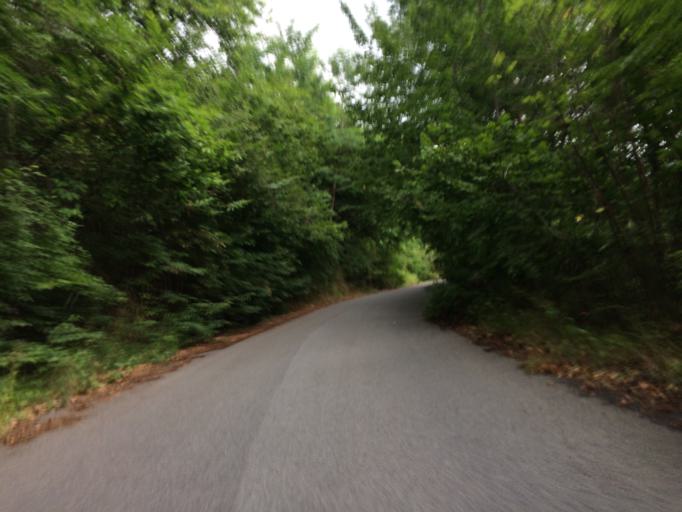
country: IT
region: Liguria
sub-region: Provincia di Imperia
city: Triora
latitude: 43.9824
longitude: 7.7592
